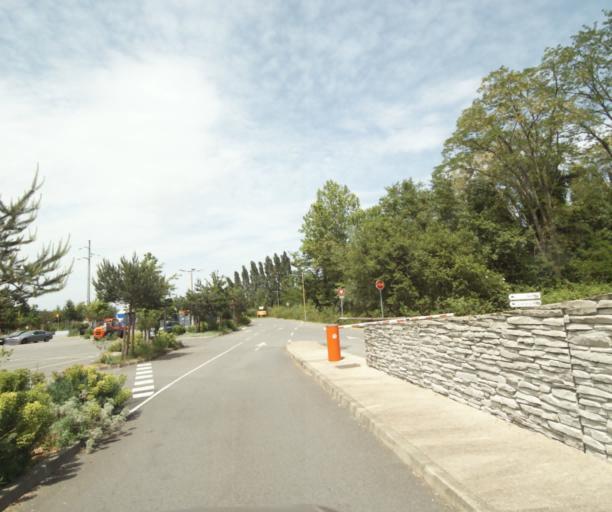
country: FR
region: Aquitaine
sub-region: Departement des Pyrenees-Atlantiques
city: Mouguerre
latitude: 43.4824
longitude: -1.4451
